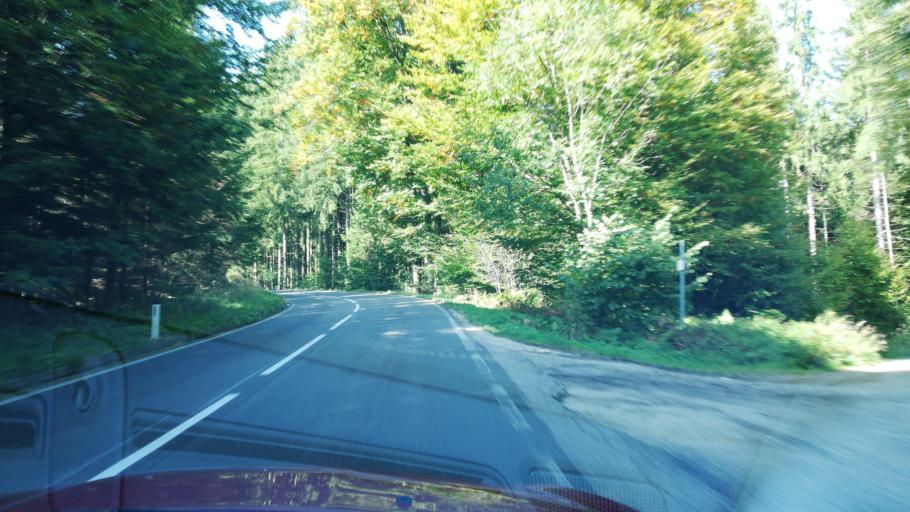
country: AT
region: Upper Austria
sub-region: Politischer Bezirk Vocklabruck
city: Redleiten
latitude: 48.1057
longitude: 13.5654
